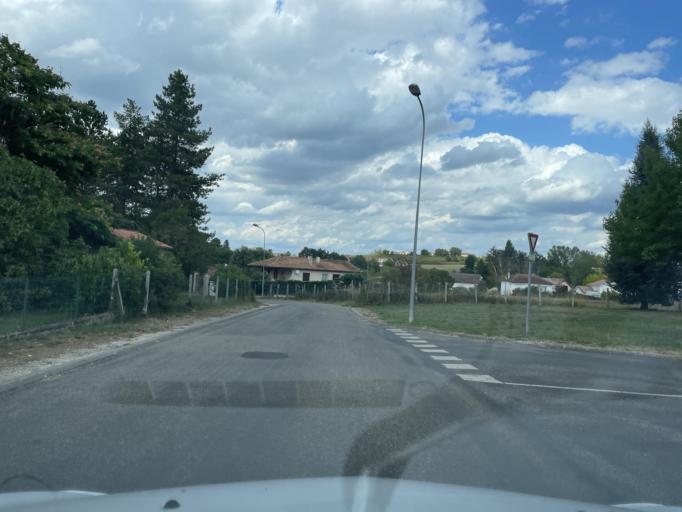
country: FR
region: Aquitaine
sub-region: Departement du Lot-et-Garonne
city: Casteljaloux
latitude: 44.3103
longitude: 0.0963
